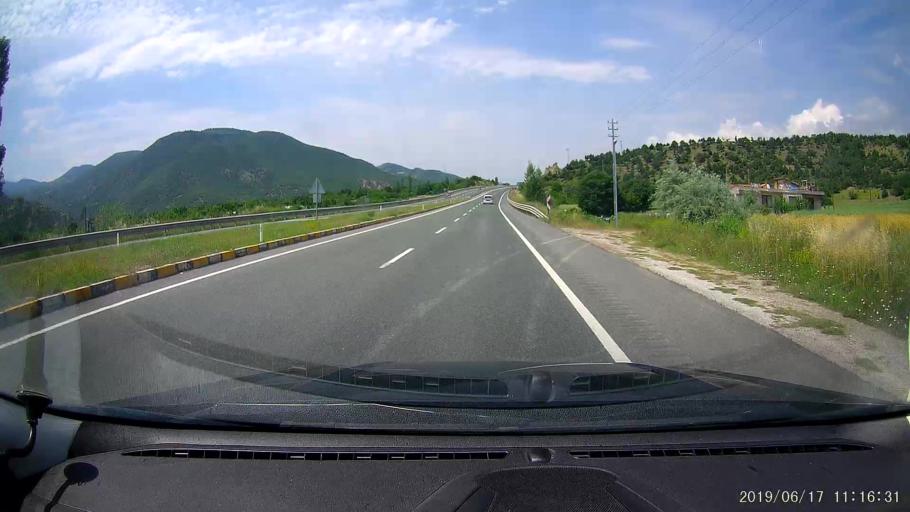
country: TR
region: Kastamonu
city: Tosya
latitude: 40.9451
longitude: 33.8982
